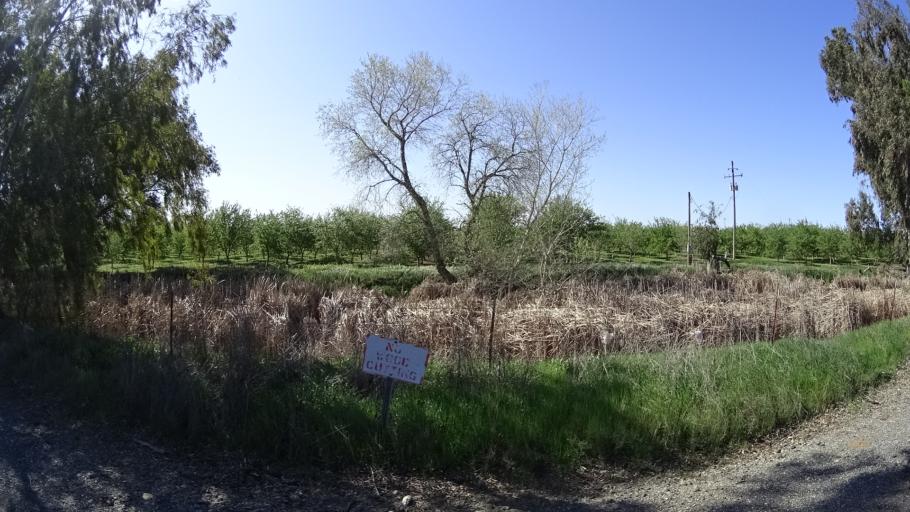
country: US
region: California
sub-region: Glenn County
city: Hamilton City
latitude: 39.7824
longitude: -122.0788
